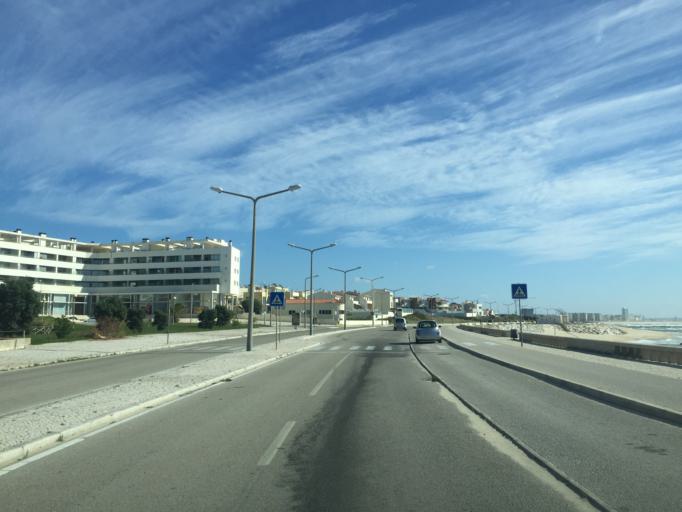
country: PT
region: Coimbra
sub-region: Figueira da Foz
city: Buarcos
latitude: 40.1710
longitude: -8.8908
